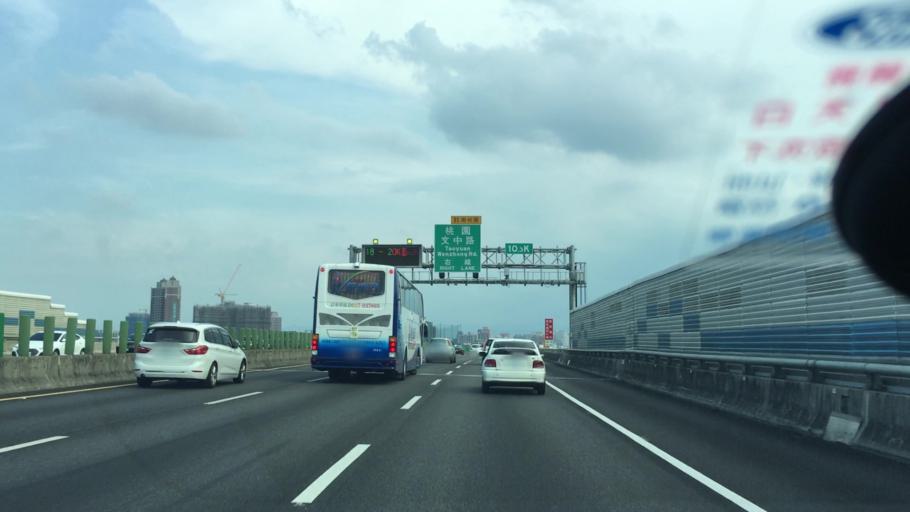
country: TW
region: Taiwan
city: Taoyuan City
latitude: 25.0101
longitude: 121.2802
